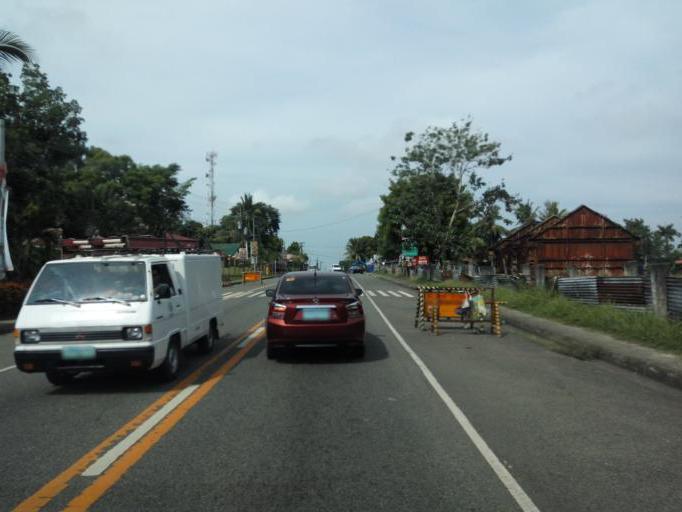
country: PH
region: Cagayan Valley
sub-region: Province of Isabela
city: Naguilian
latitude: 17.0123
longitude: 121.8452
